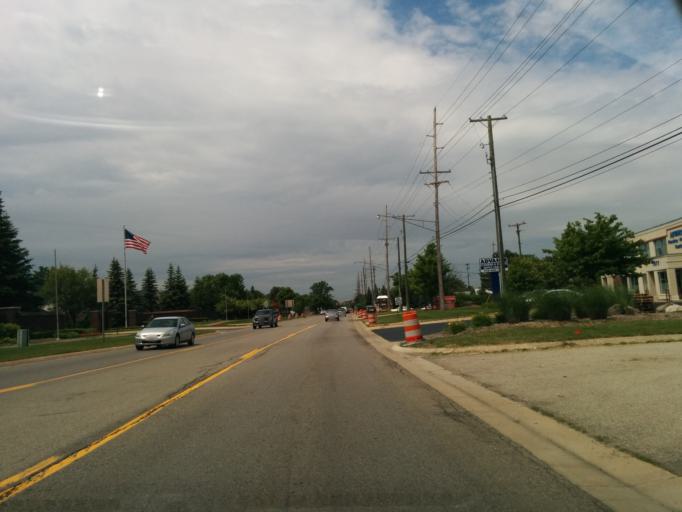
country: US
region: Michigan
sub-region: Oakland County
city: Walled Lake
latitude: 42.5403
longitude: -83.4629
